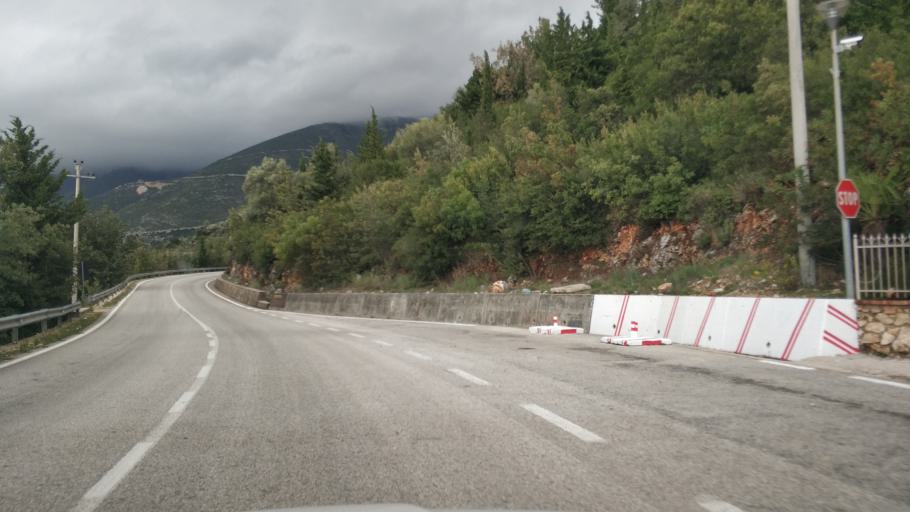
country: AL
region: Vlore
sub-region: Rrethi i Vlores
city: Vranisht
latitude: 40.1678
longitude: 19.6190
